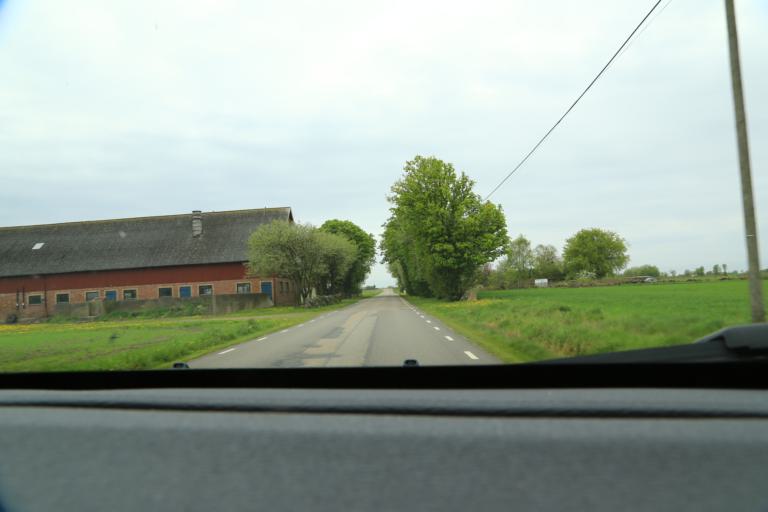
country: SE
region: Halland
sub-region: Varbergs Kommun
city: Tvaaker
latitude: 57.0354
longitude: 12.3476
